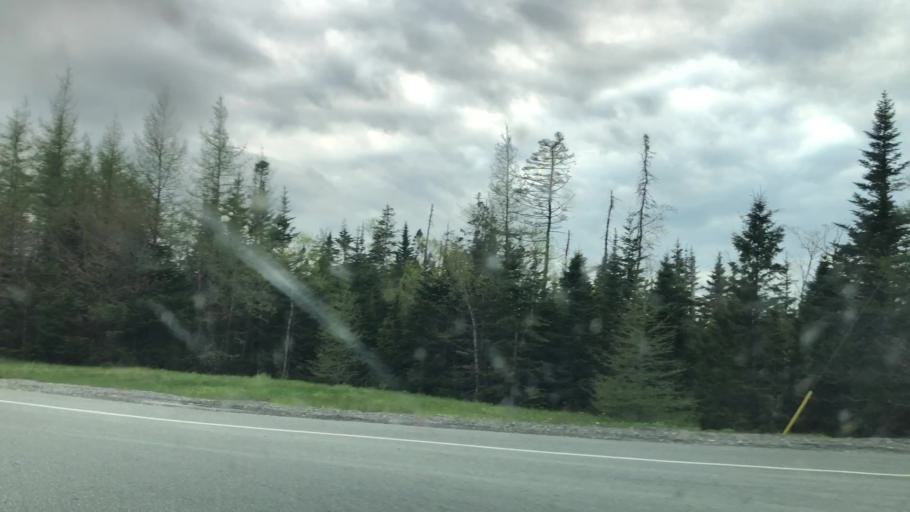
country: CA
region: Nova Scotia
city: Cole Harbour
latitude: 44.7815
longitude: -63.1777
